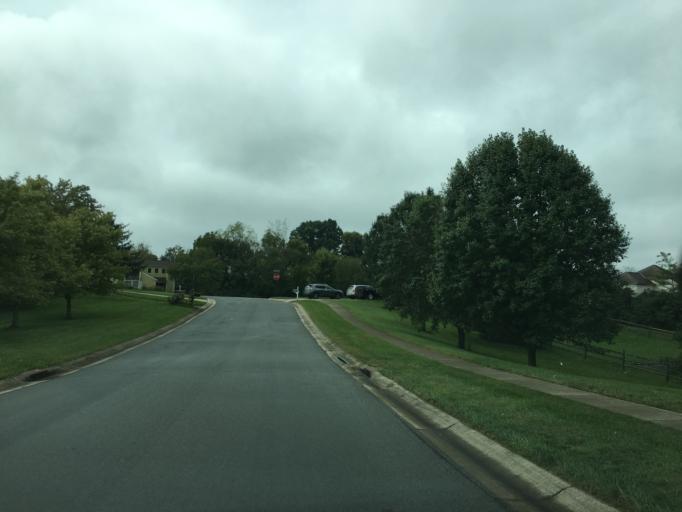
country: US
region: Ohio
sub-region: Butler County
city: Beckett Ridge
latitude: 39.3591
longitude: -84.4454
